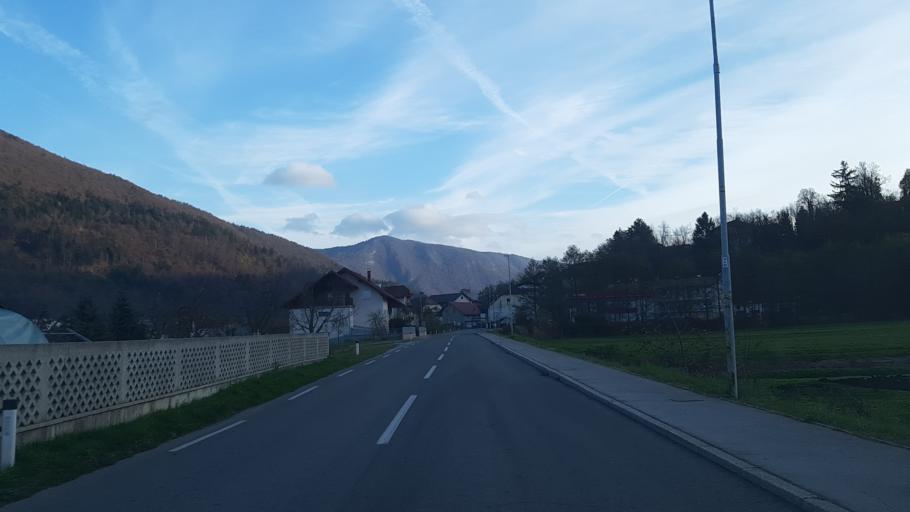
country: SI
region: Borovnica
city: Borovnica
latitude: 45.9228
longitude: 14.3592
